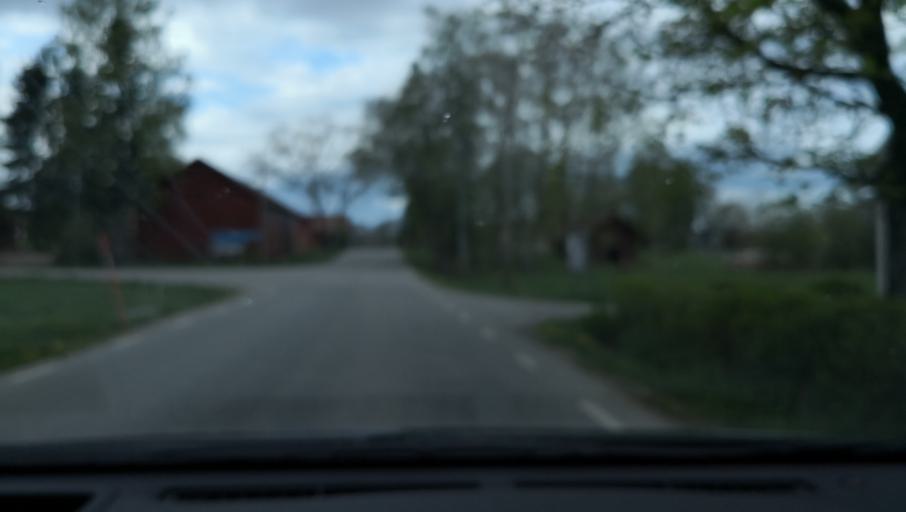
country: SE
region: Dalarna
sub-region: Avesta Kommun
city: Avesta
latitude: 60.0220
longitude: 16.2708
